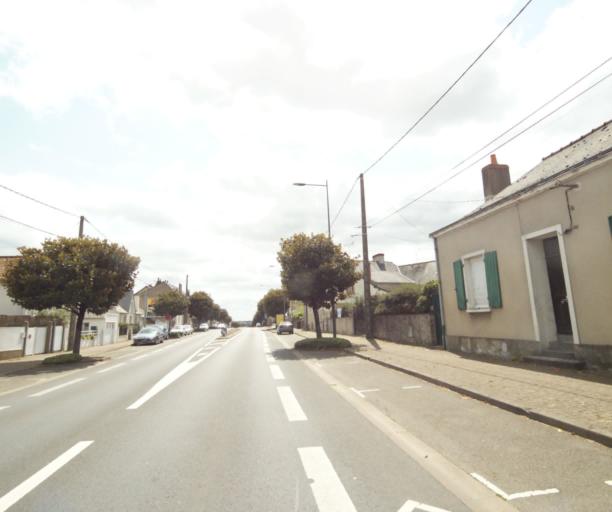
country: FR
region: Pays de la Loire
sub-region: Departement de la Sarthe
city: Sable-sur-Sarthe
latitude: 47.8472
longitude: -0.3468
